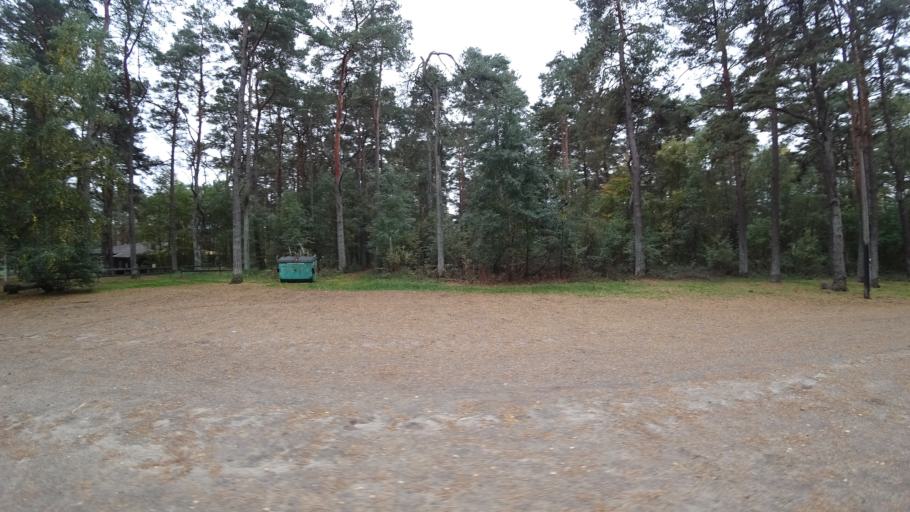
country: SE
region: Skane
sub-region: Kavlinge Kommun
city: Hofterup
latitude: 55.8192
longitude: 12.9527
